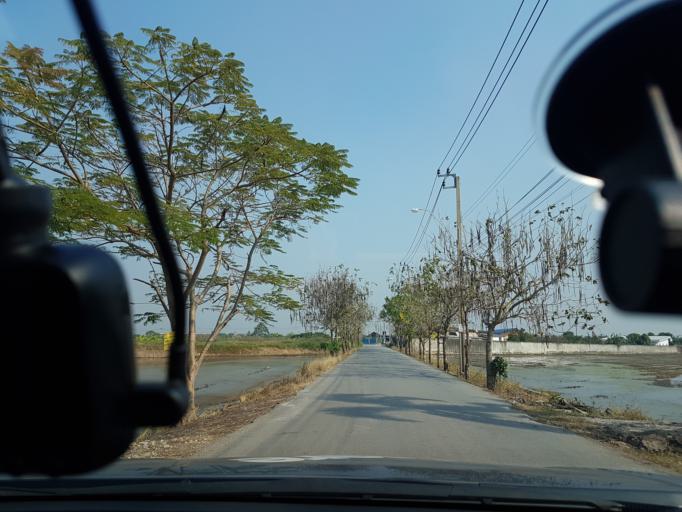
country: TH
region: Pathum Thani
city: Lam Luk Ka
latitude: 13.9133
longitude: 100.7103
